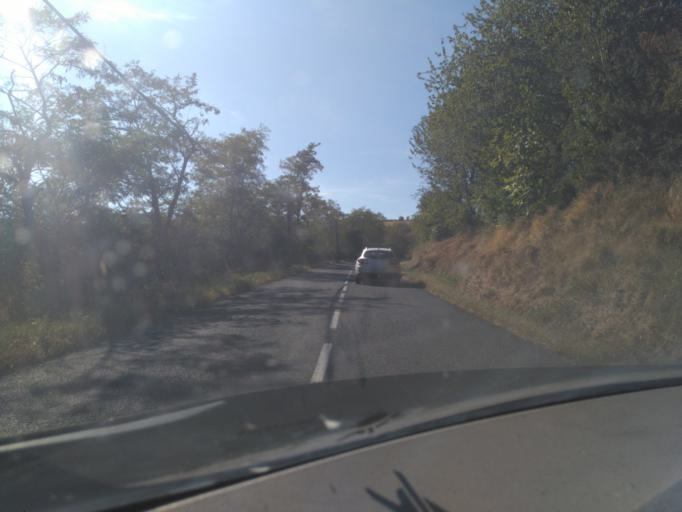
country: FR
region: Rhone-Alpes
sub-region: Departement du Rhone
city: Tarare
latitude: 45.8752
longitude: 4.4250
